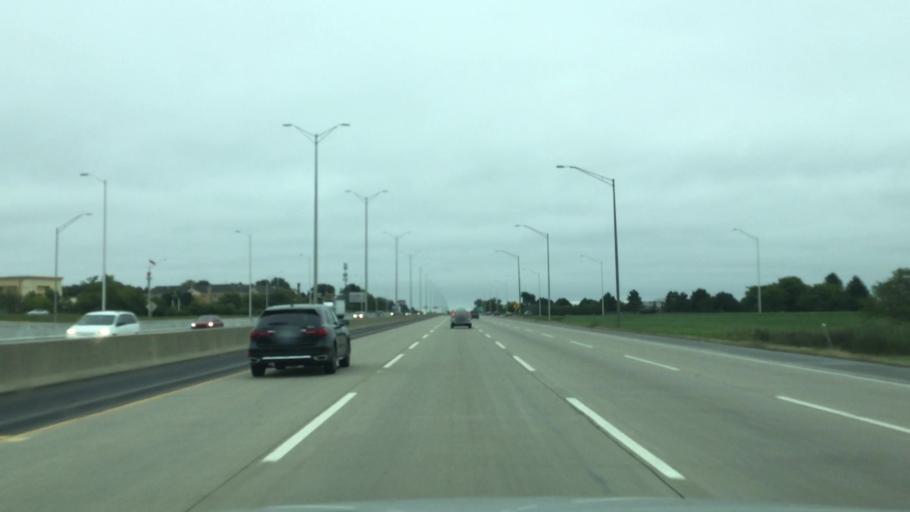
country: US
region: Illinois
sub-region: Lake County
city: Grandwood Park
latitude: 42.3800
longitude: -87.9471
